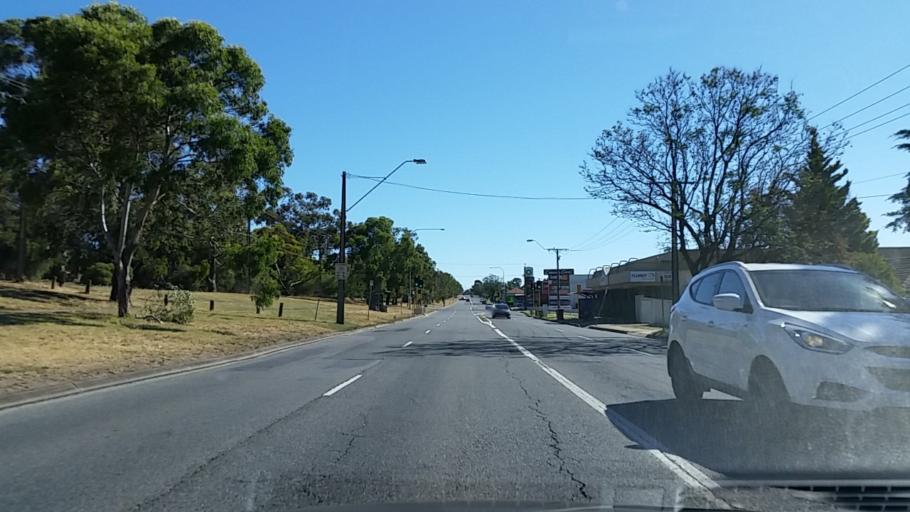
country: AU
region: South Australia
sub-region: Salisbury
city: Ingle Farm
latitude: -34.8269
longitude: 138.6333
